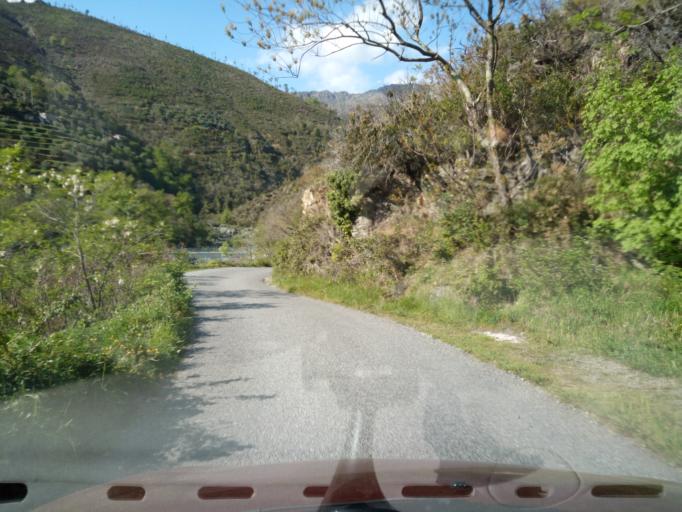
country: IT
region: Liguria
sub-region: Provincia di Genova
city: Sciarborasca
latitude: 44.3978
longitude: 8.6040
